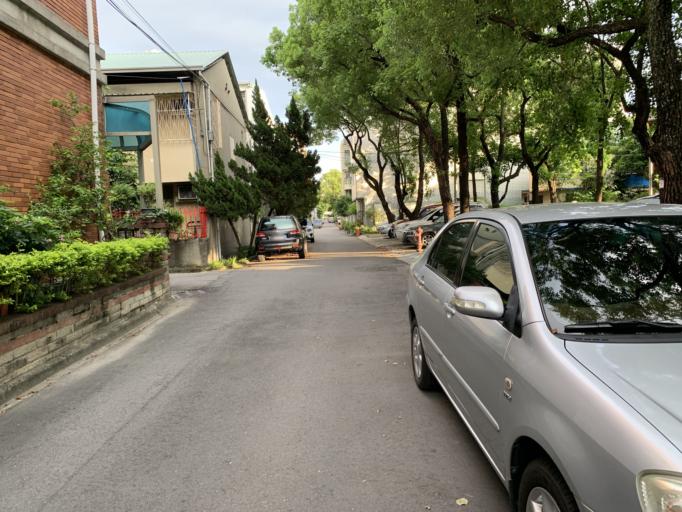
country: TW
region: Taiwan
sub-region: Taichung City
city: Taichung
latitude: 24.1546
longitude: 120.6308
